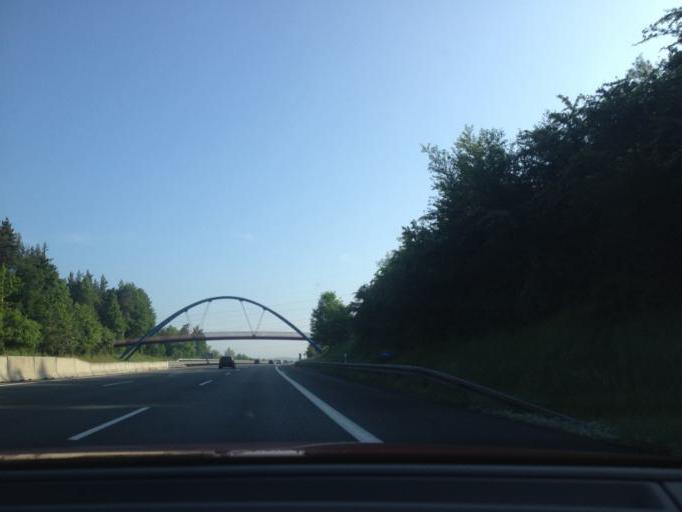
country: DE
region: Bavaria
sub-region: Regierungsbezirk Mittelfranken
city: Schnaittach
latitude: 49.5586
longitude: 11.3249
